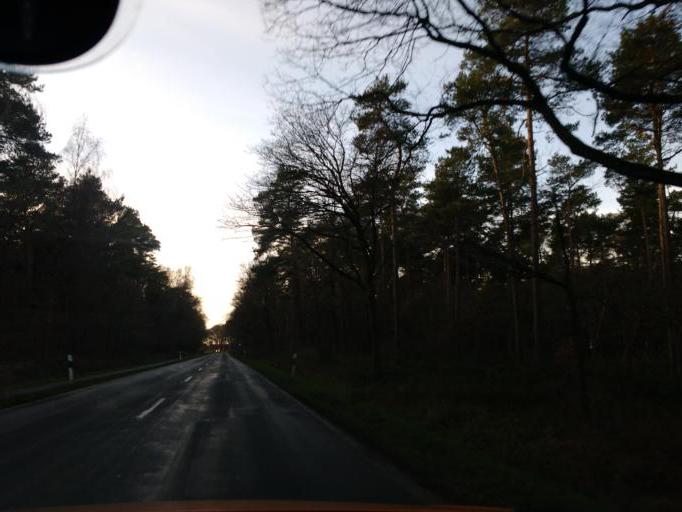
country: DE
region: Lower Saxony
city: Hatten
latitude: 53.0941
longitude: 8.4115
